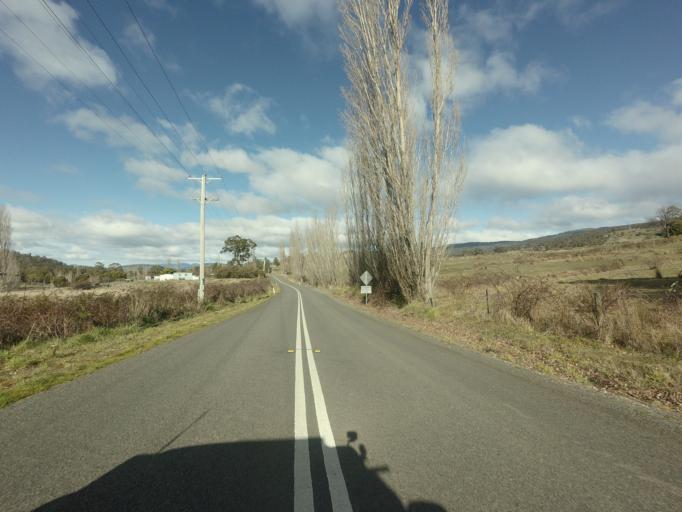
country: AU
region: Tasmania
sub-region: Derwent Valley
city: New Norfolk
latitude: -42.6582
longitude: 146.7734
